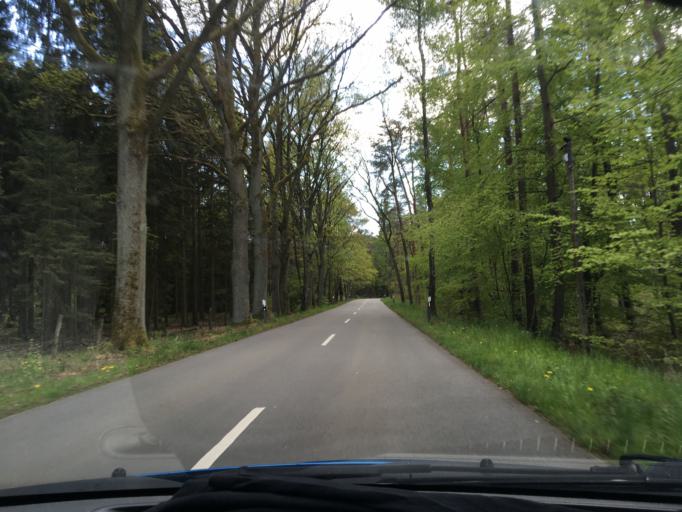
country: DE
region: Lower Saxony
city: Nahrendorf
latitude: 53.1501
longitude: 10.8128
